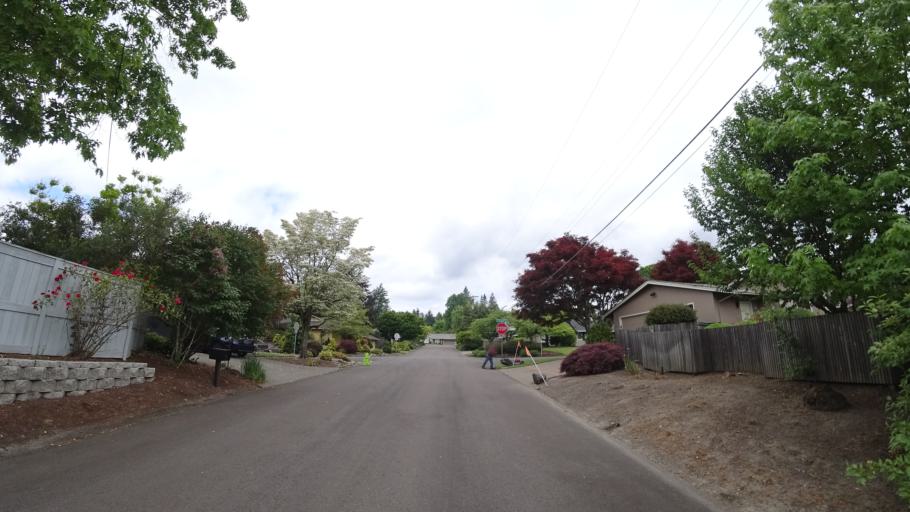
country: US
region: Oregon
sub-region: Washington County
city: Raleigh Hills
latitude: 45.4790
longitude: -122.7537
